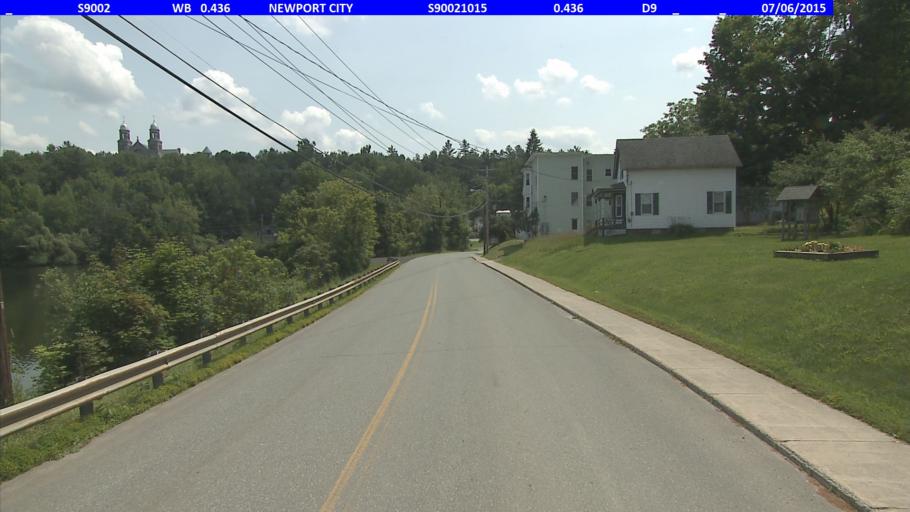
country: US
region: Vermont
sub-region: Orleans County
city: Newport
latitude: 44.9347
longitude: -72.2173
